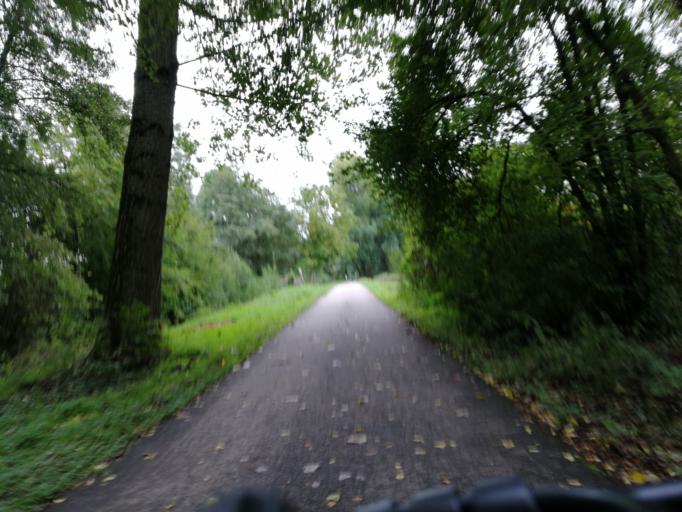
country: DE
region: North Rhine-Westphalia
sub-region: Regierungsbezirk Dusseldorf
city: Neuss
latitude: 51.1444
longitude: 6.7383
